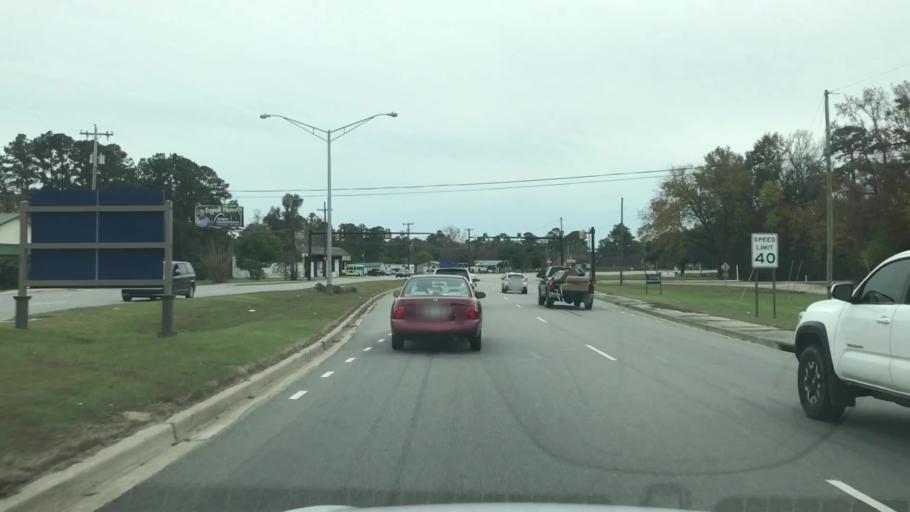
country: US
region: South Carolina
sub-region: Georgetown County
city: Georgetown
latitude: 33.3532
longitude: -79.2930
